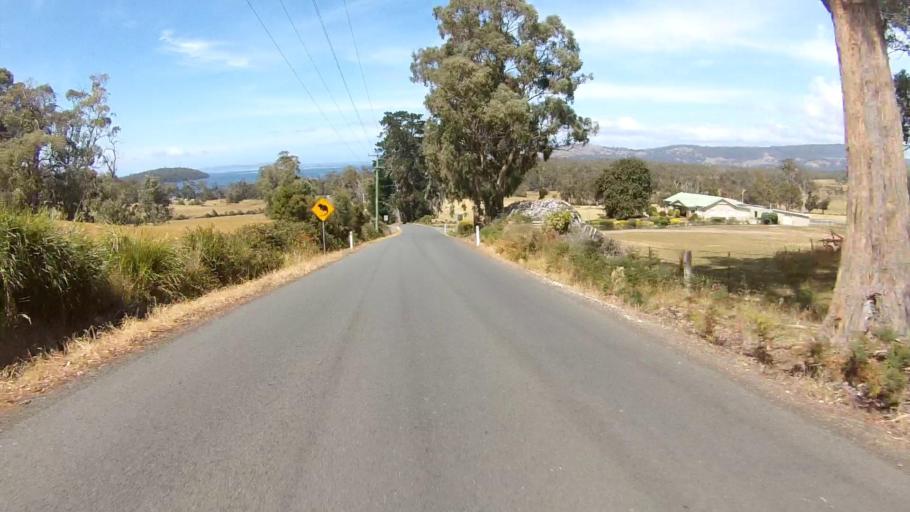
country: AU
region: Tasmania
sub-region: Huon Valley
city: Cygnet
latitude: -43.2341
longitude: 147.1261
